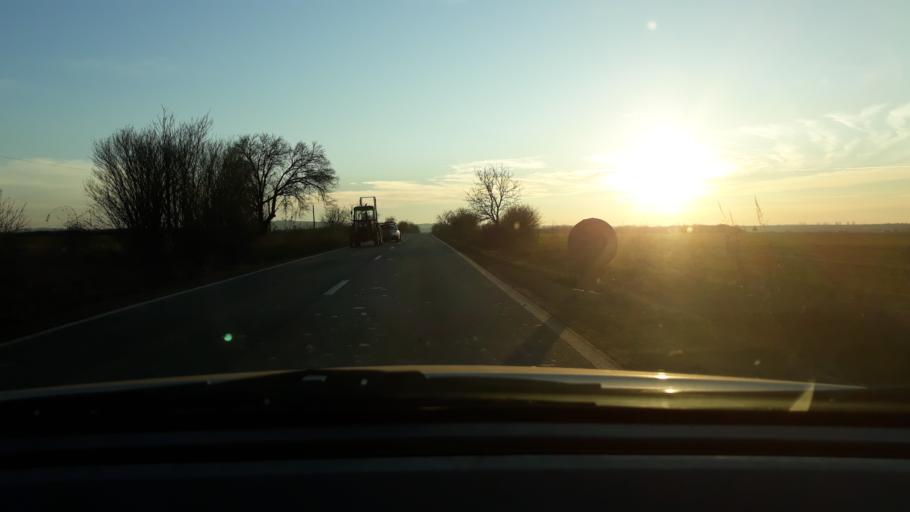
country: RO
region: Bihor
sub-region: Comuna Spinus
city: Spinus
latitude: 47.2436
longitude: 22.1999
